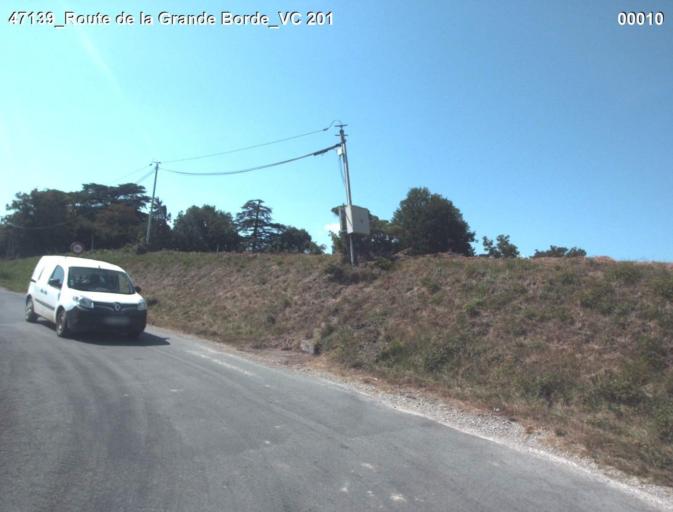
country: FR
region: Aquitaine
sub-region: Departement du Lot-et-Garonne
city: Nerac
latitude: 44.0634
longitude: 0.3944
